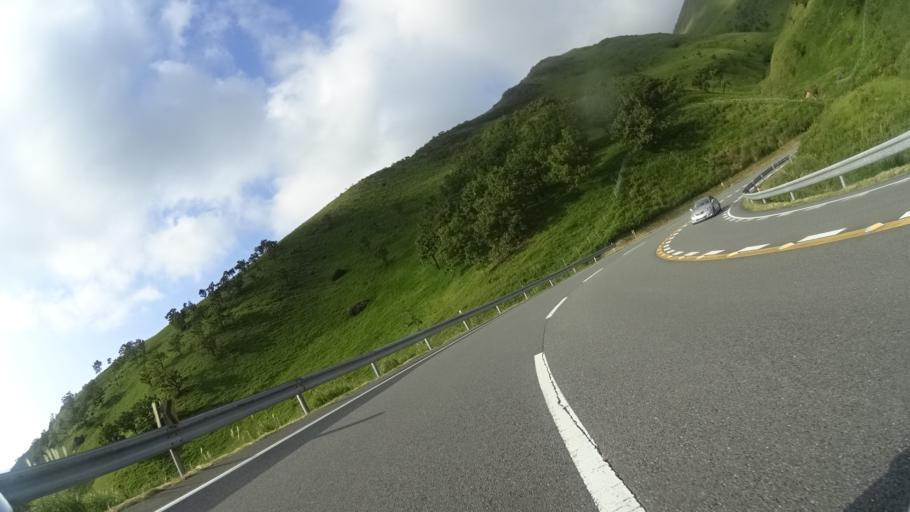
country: JP
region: Oita
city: Beppu
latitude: 33.2645
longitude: 131.3824
